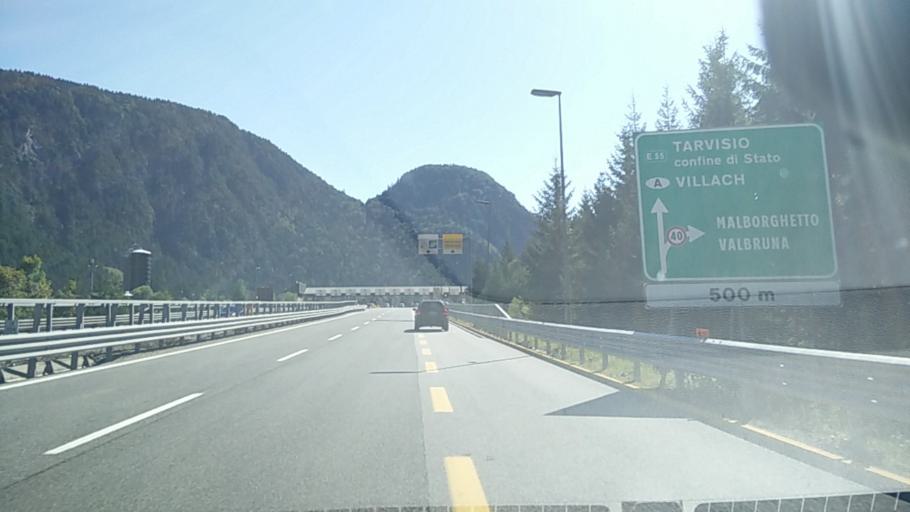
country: IT
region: Friuli Venezia Giulia
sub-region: Provincia di Udine
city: Malborghetto
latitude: 46.5067
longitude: 13.4766
